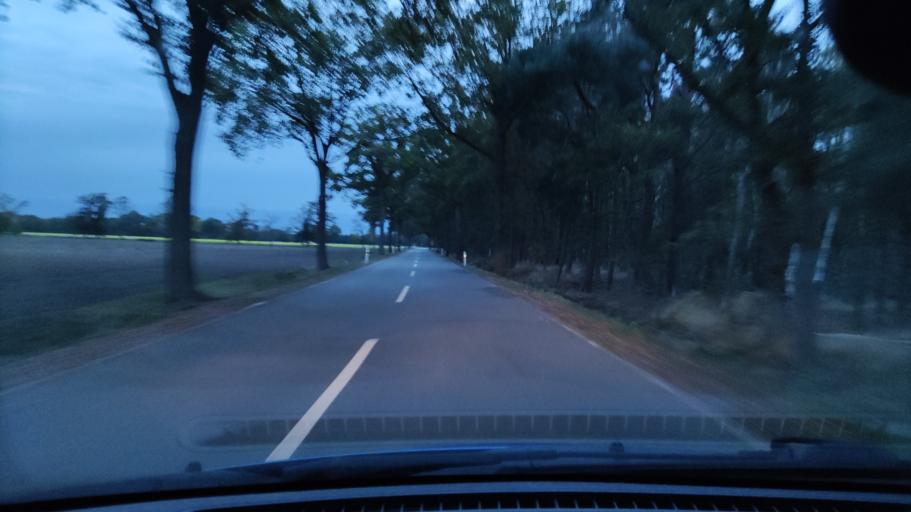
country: DE
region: Lower Saxony
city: Trebel
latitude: 52.9695
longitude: 11.2826
